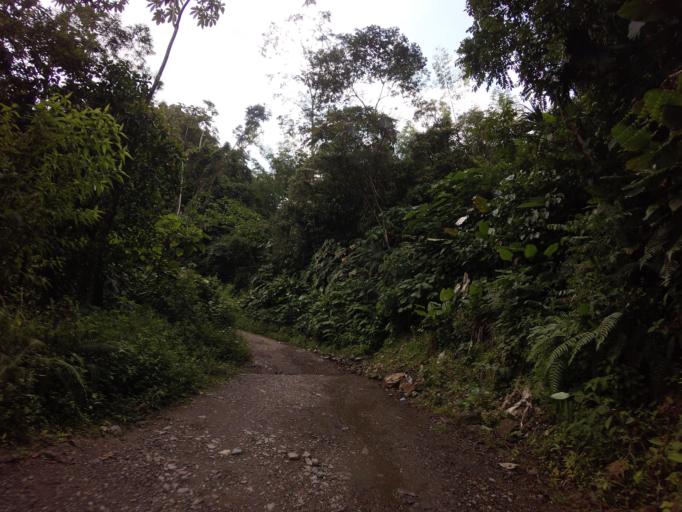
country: CO
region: Antioquia
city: Narino
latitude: 5.5129
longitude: -75.1934
